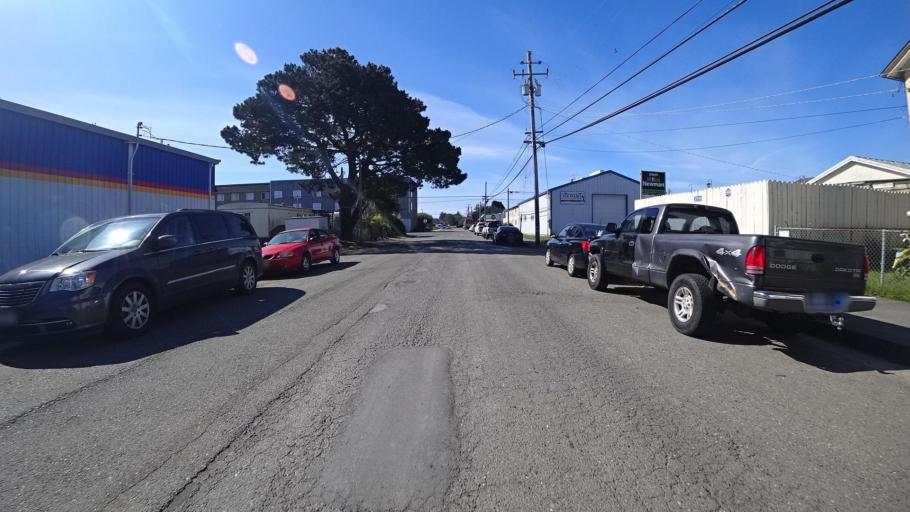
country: US
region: California
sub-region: Humboldt County
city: Eureka
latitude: 40.8061
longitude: -124.1515
